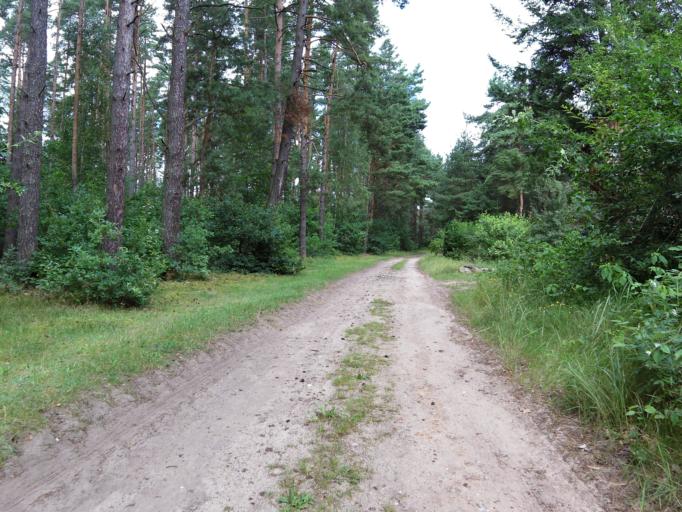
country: DE
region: Brandenburg
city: Lychen
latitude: 53.2194
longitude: 13.2748
